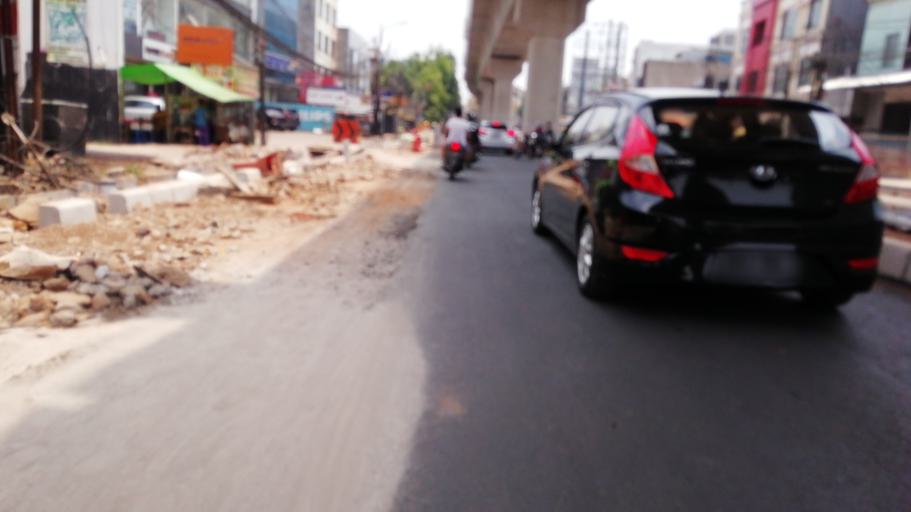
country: ID
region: Jakarta Raya
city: Jakarta
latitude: -6.2701
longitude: 106.7974
